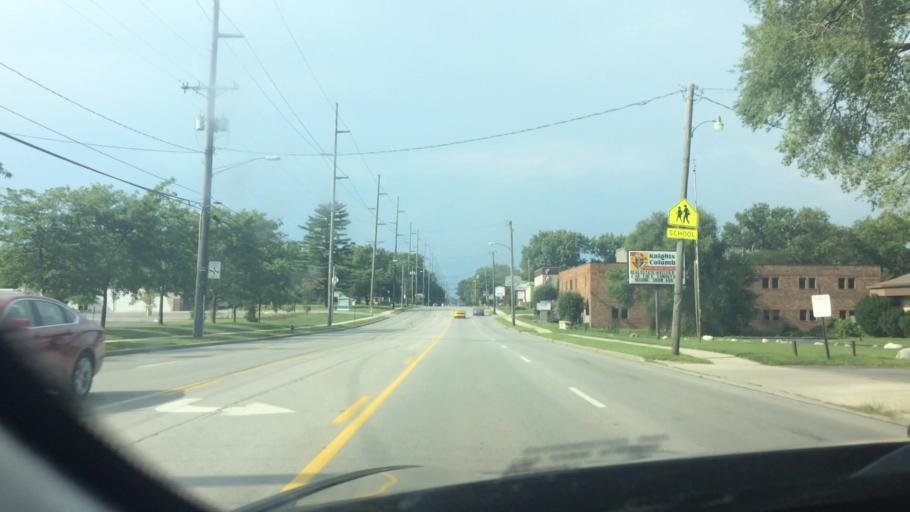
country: US
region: Ohio
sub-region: Lucas County
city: Ottawa Hills
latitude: 41.6959
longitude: -83.6233
